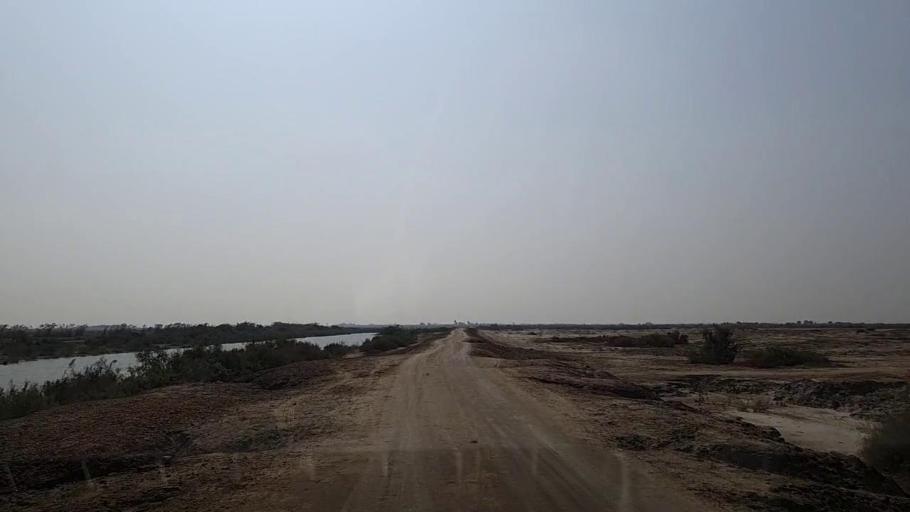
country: PK
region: Sindh
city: Gharo
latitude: 24.6796
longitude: 67.7345
